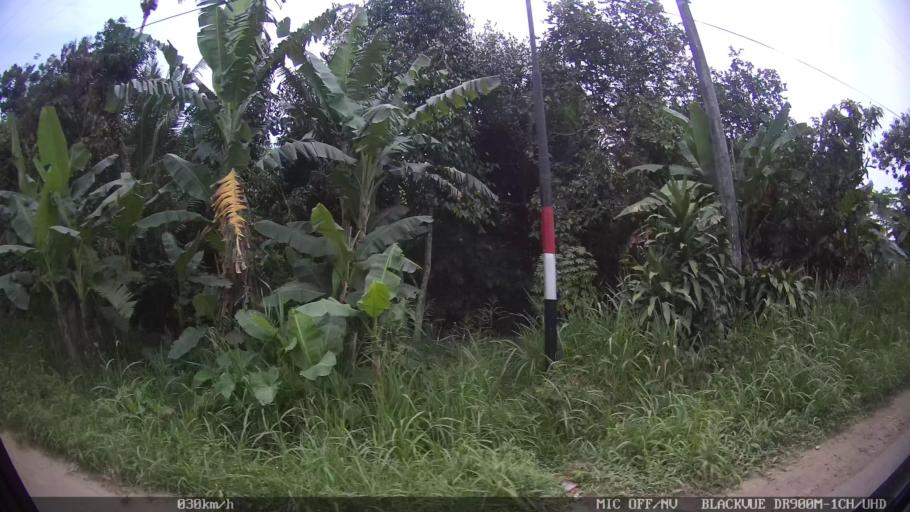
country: ID
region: Lampung
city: Panjang
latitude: -5.4179
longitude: 105.3490
